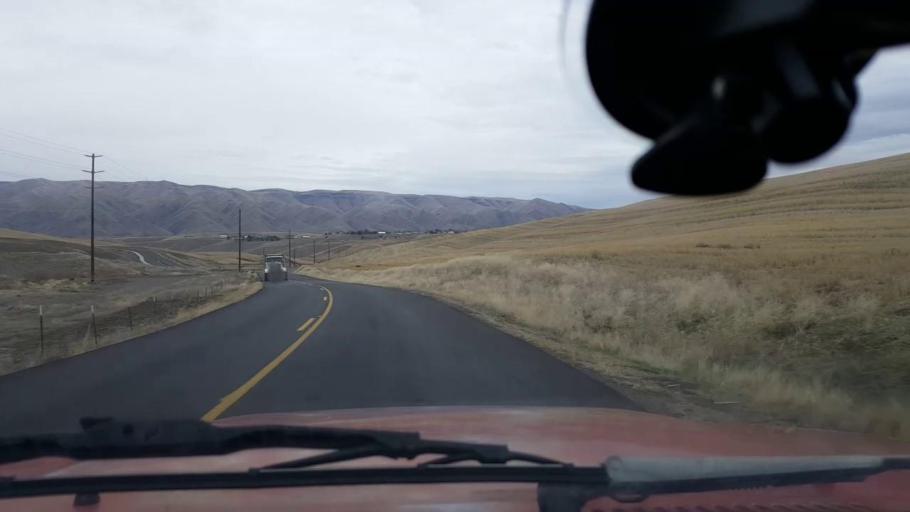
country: US
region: Washington
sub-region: Asotin County
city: Clarkston Heights-Vineland
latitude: 46.3907
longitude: -117.1062
